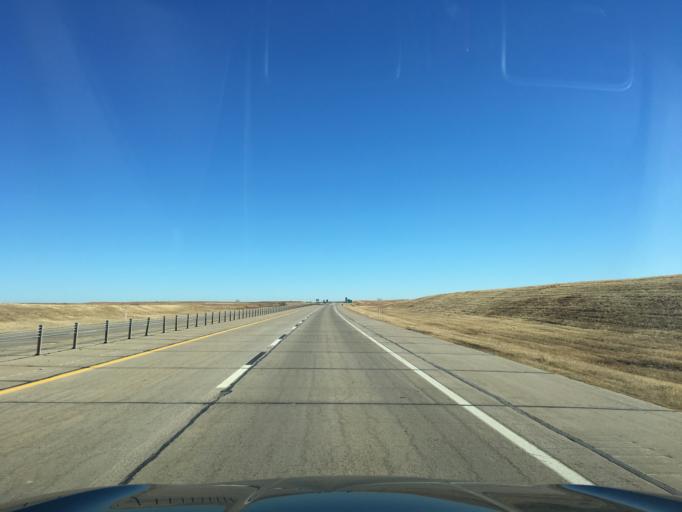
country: US
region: Oklahoma
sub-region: Noble County
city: Perry
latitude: 36.4001
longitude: -97.3156
